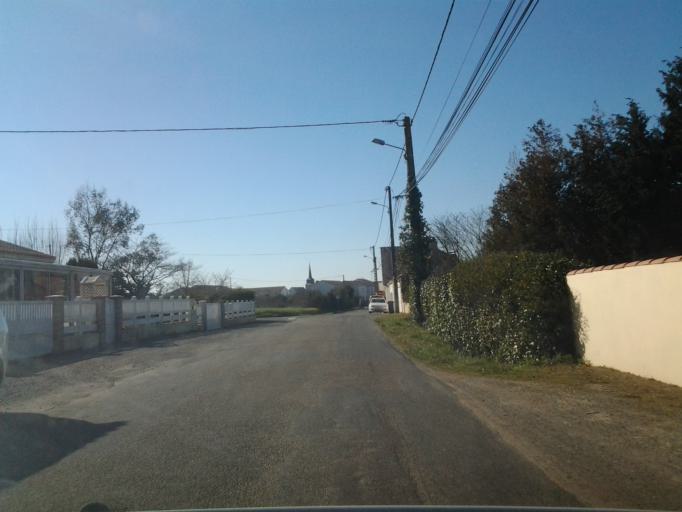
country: FR
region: Pays de la Loire
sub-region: Departement de la Vendee
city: Olonne-sur-Mer
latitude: 46.5378
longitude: -1.7652
